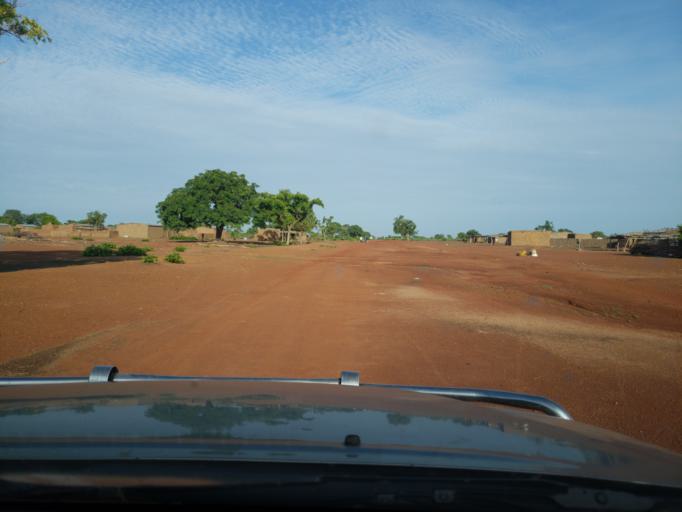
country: ML
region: Sikasso
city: Koutiala
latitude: 12.4287
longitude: -5.6215
